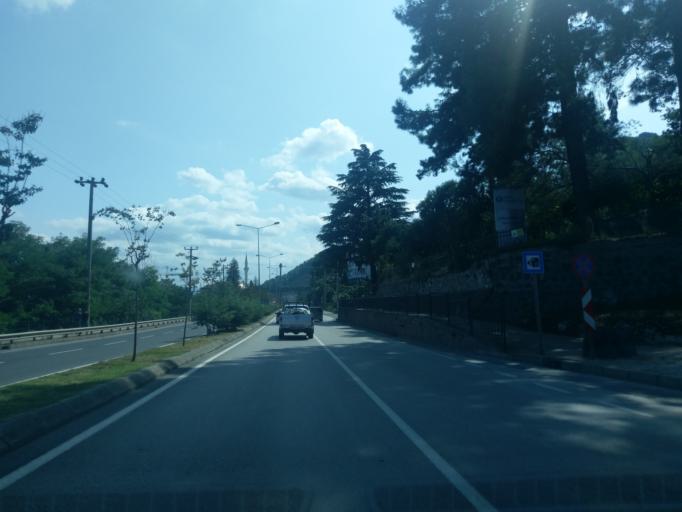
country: TR
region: Ordu
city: Ordu
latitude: 41.0060
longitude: 37.8696
